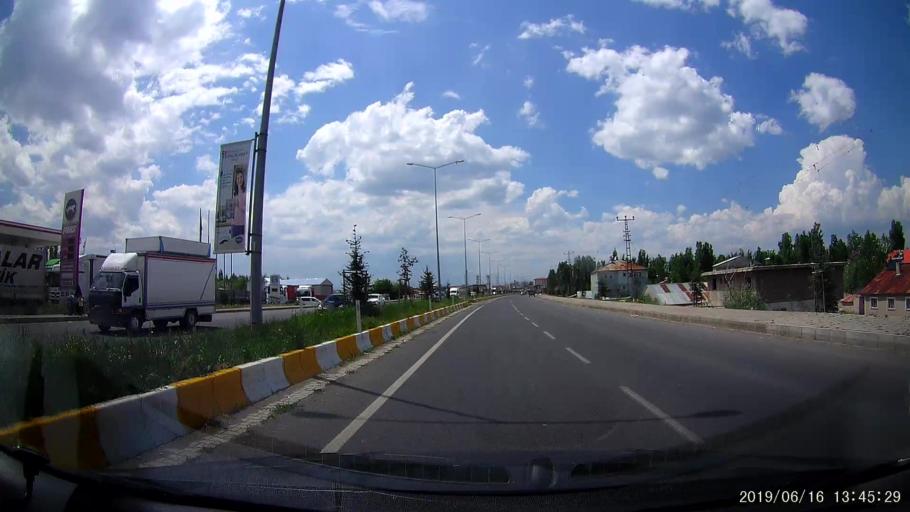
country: TR
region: Agri
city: Agri
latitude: 39.7089
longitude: 43.0452
